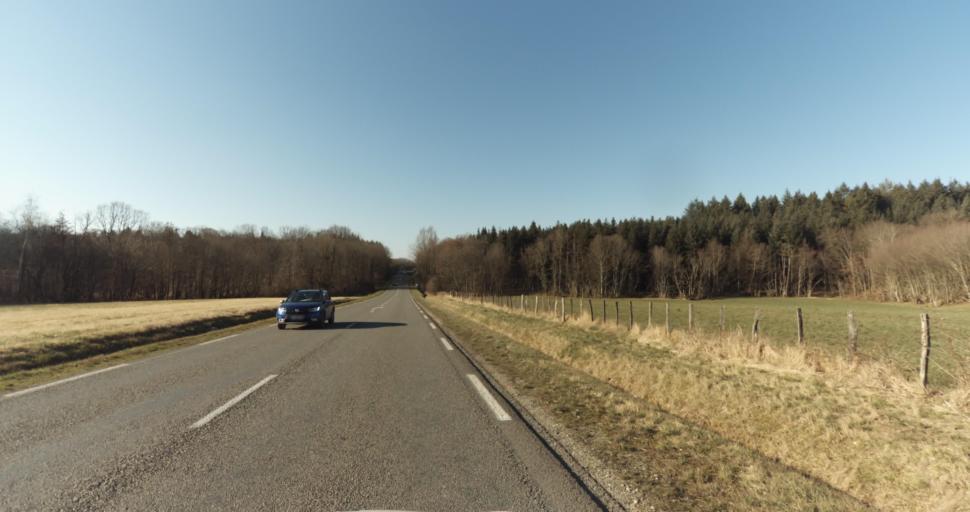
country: FR
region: Franche-Comte
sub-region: Departement du Jura
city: Montmorot
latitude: 46.6955
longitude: 5.4935
